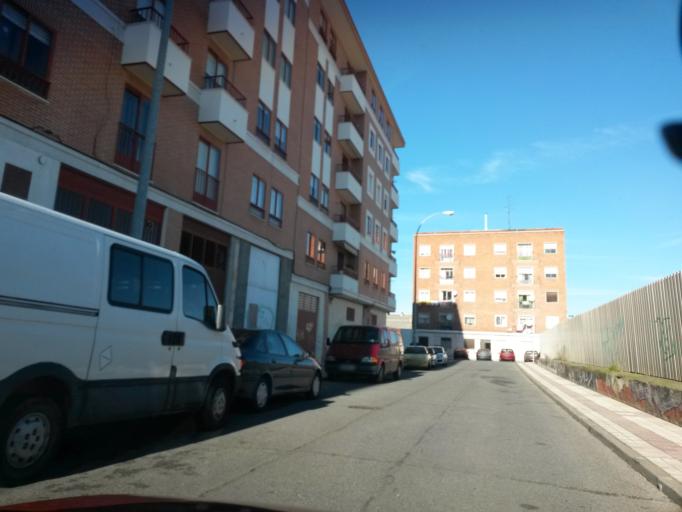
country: ES
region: Castille and Leon
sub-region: Provincia de Salamanca
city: Salamanca
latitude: 40.9744
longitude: -5.6460
